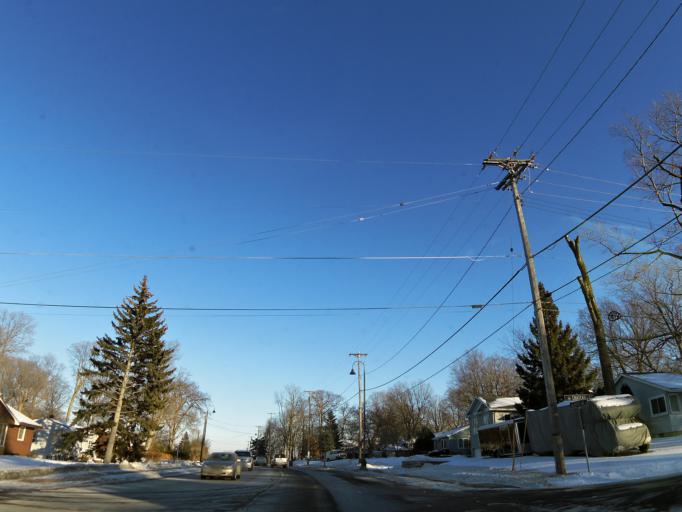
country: US
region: Minnesota
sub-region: Hennepin County
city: Mound
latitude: 44.9366
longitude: -93.6537
